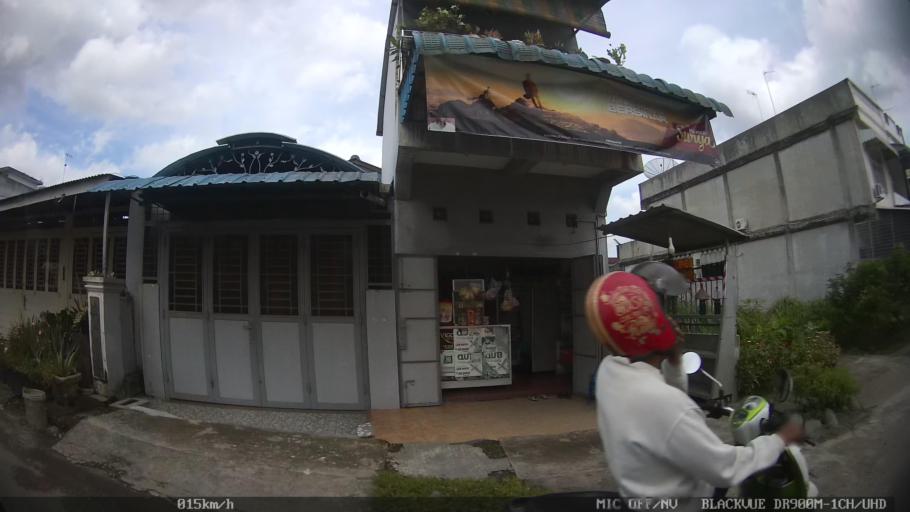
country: ID
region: North Sumatra
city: Percut
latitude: 3.5659
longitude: 98.8764
